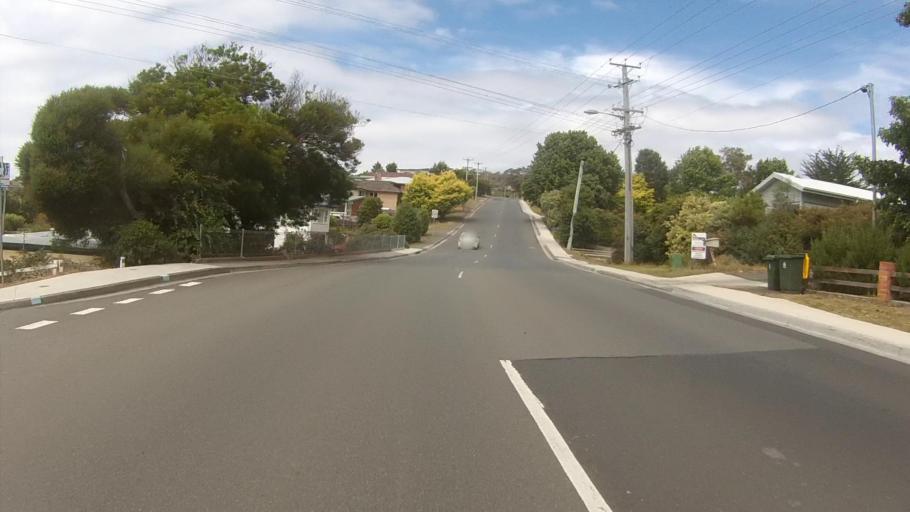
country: AU
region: Tasmania
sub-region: Kingborough
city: Blackmans Bay
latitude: -43.0037
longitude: 147.3191
